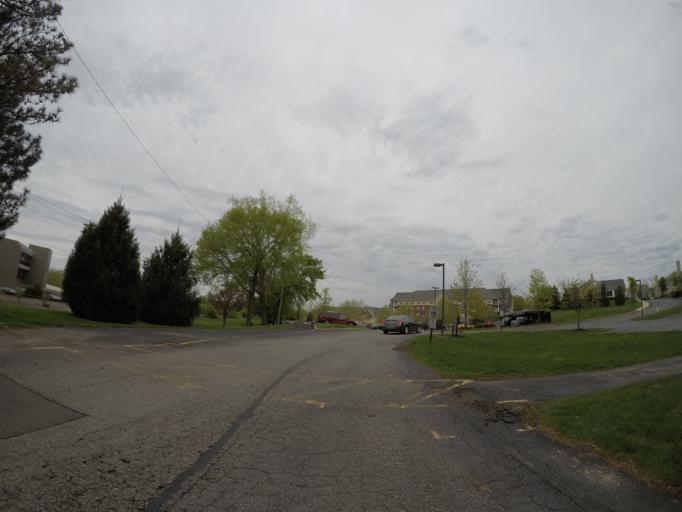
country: US
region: Ohio
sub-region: Franklin County
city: Upper Arlington
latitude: 39.9903
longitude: -83.0647
